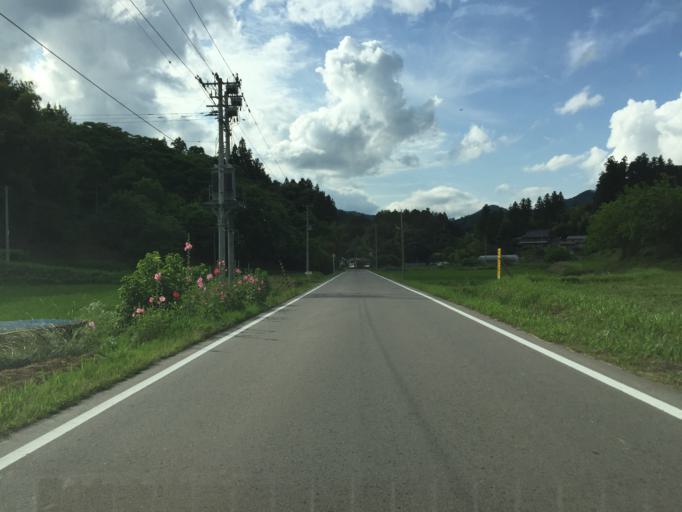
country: JP
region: Fukushima
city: Fukushima-shi
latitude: 37.6812
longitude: 140.5730
